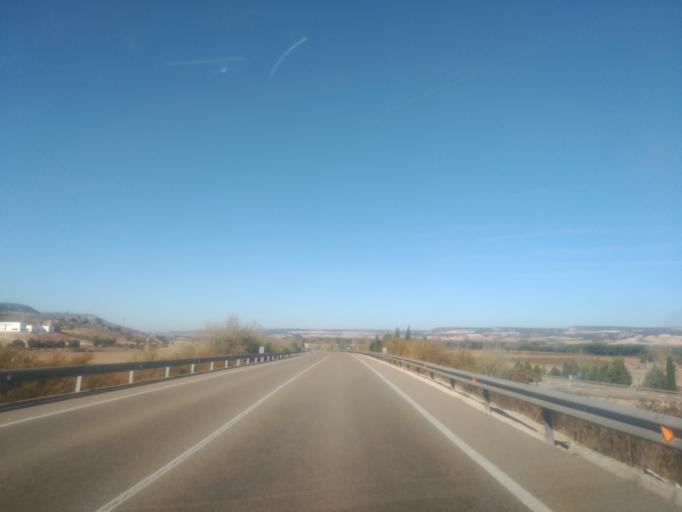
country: ES
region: Castille and Leon
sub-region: Provincia de Valladolid
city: Quintanilla de Arriba
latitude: 41.6185
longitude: -4.2253
